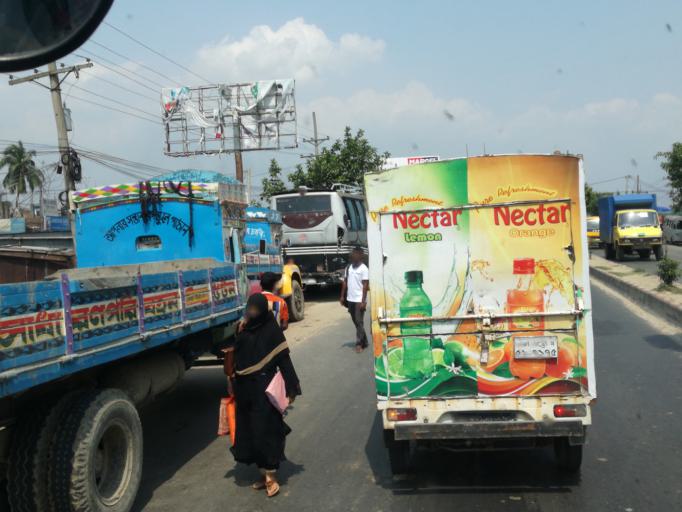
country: BD
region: Dhaka
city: Azimpur
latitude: 23.7952
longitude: 90.2901
